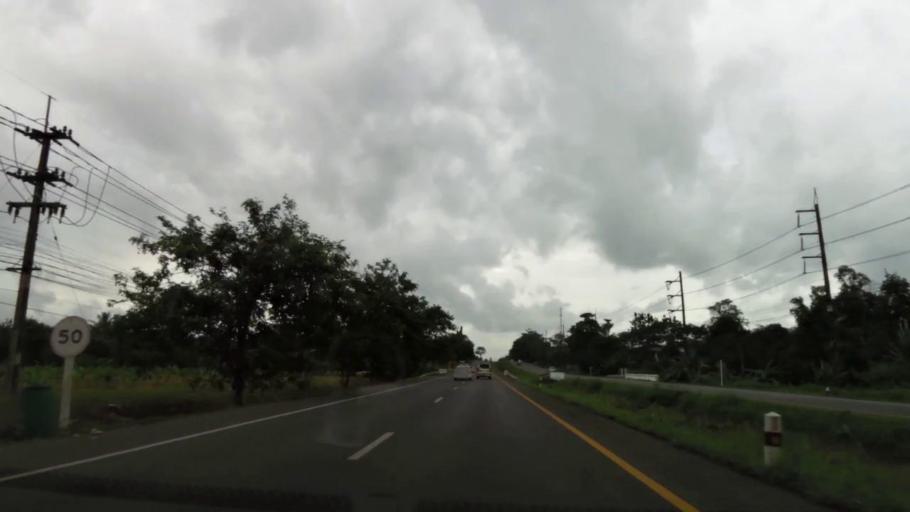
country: TH
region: Chanthaburi
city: Tha Mai
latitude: 12.6837
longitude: 102.0037
